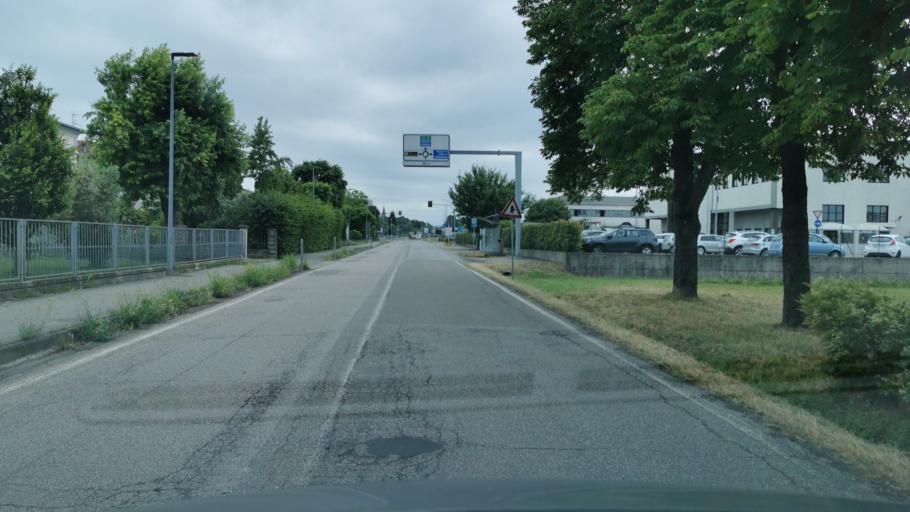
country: IT
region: Emilia-Romagna
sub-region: Provincia di Parma
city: Soragna
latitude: 44.9221
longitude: 10.1145
